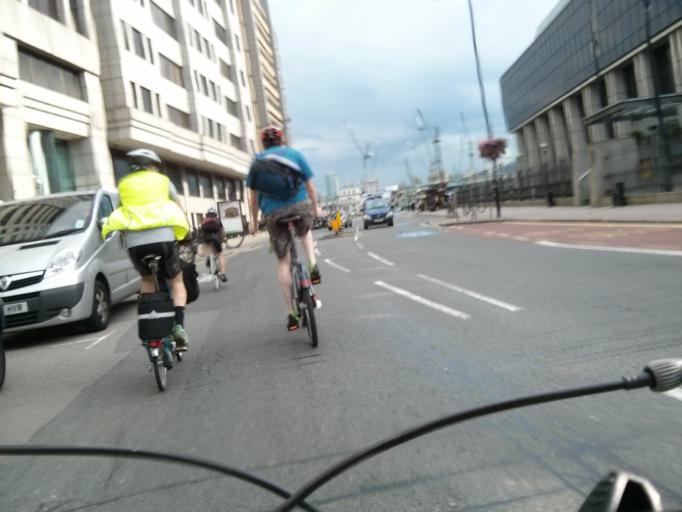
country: GB
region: England
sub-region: Greater London
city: City of London
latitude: 51.5071
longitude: -0.0950
